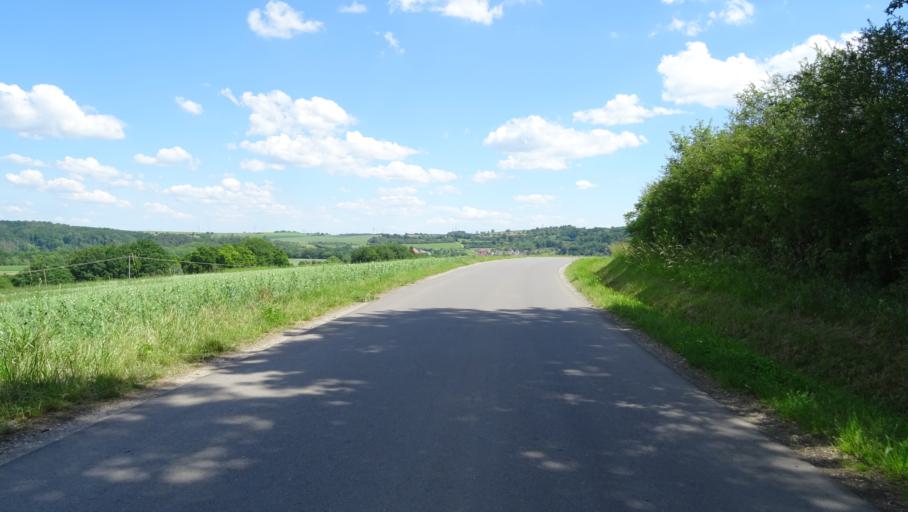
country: DE
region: Baden-Wuerttemberg
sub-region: Karlsruhe Region
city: Adelsheim
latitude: 49.3883
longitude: 9.3730
